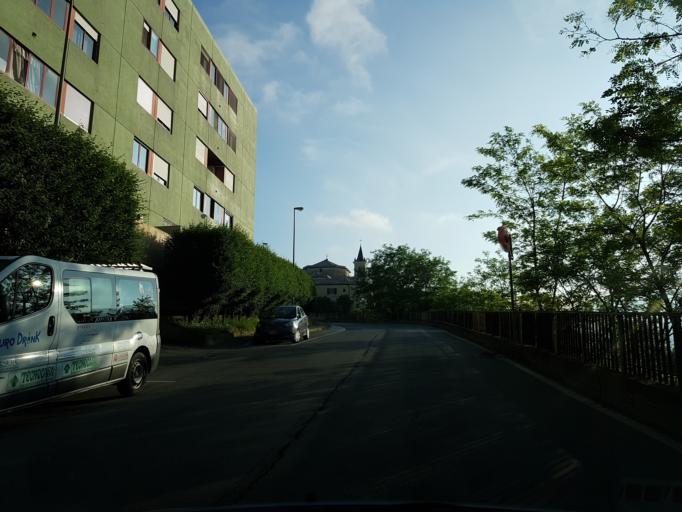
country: IT
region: Liguria
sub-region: Provincia di Genova
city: Genoa
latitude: 44.4503
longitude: 8.9078
